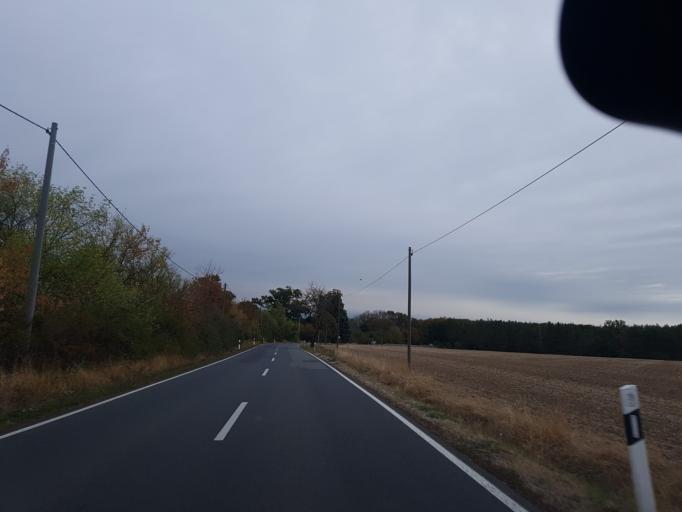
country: DE
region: Saxony
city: Beilrode
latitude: 51.6097
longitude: 13.0393
